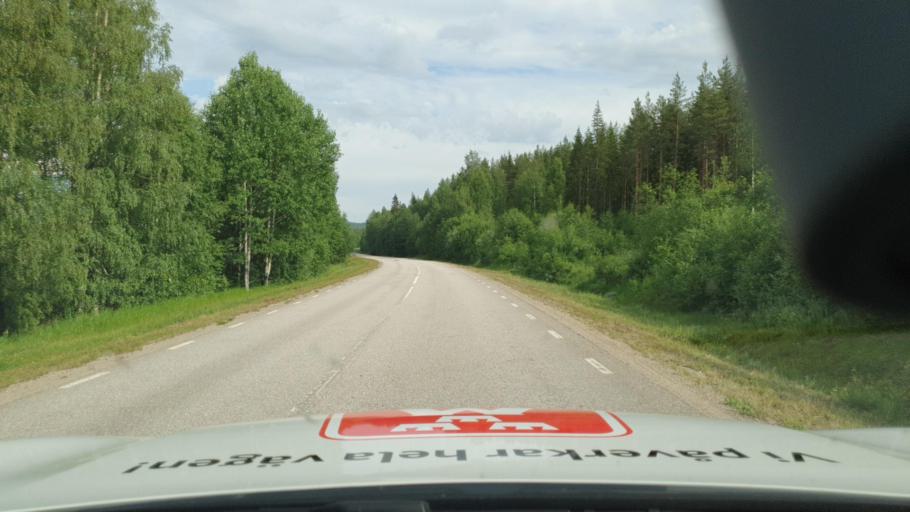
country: NO
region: Hedmark
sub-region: Trysil
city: Innbygda
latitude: 60.9128
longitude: 12.5493
